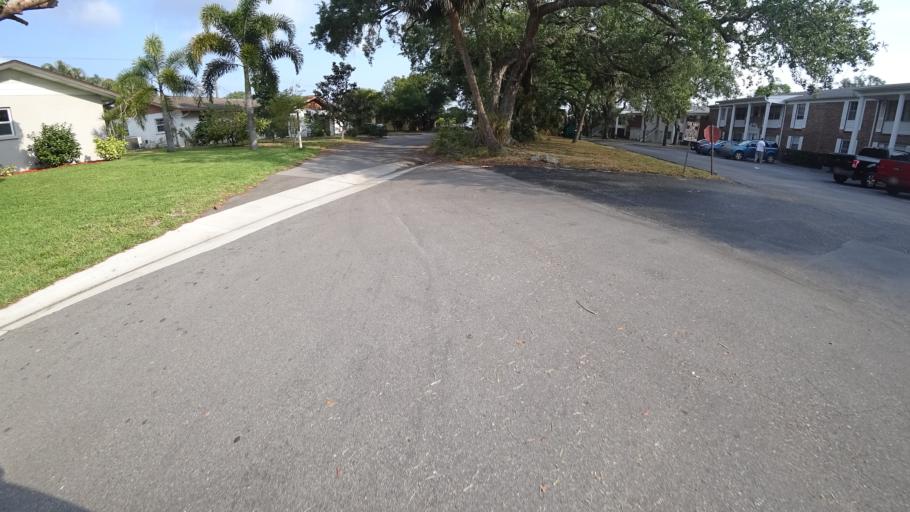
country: US
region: Florida
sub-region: Manatee County
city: South Bradenton
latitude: 27.4590
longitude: -82.5712
